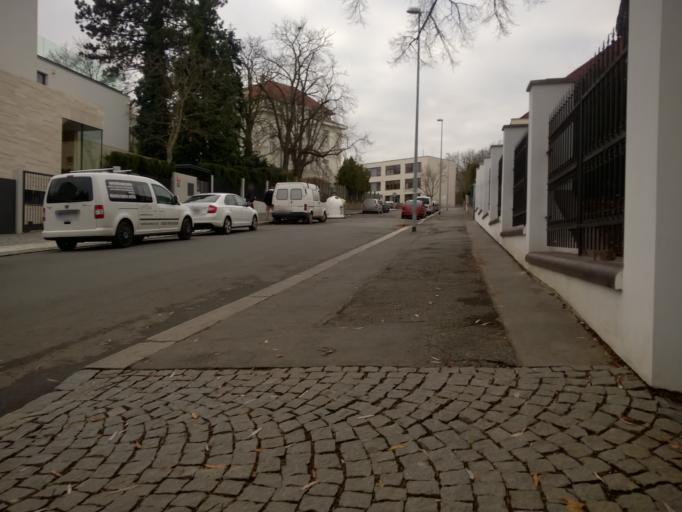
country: CZ
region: Praha
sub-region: Praha 1
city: Mala Strana
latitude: 50.1064
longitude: 14.4035
